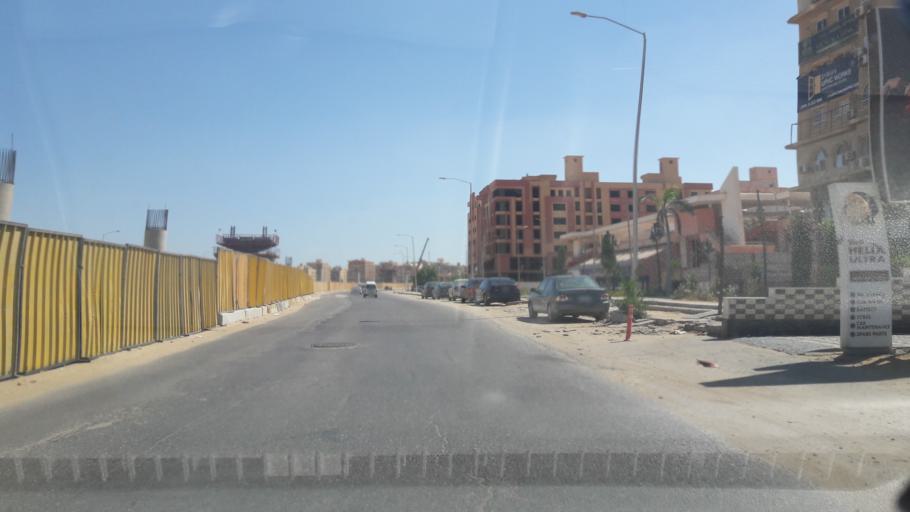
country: EG
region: Al Jizah
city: Madinat Sittah Uktubar
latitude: 29.9659
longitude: 30.9302
